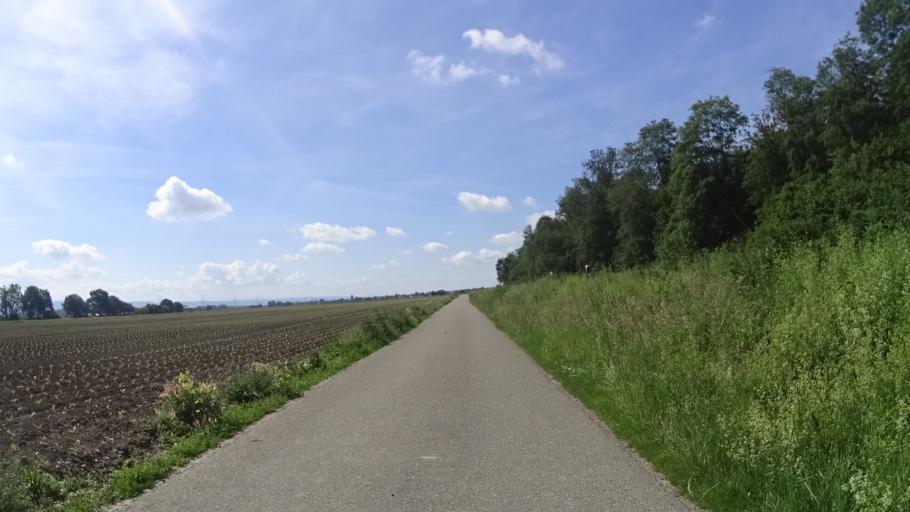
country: DE
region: Baden-Wuerttemberg
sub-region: Freiburg Region
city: Schutterwald
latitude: 48.4821
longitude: 7.8174
